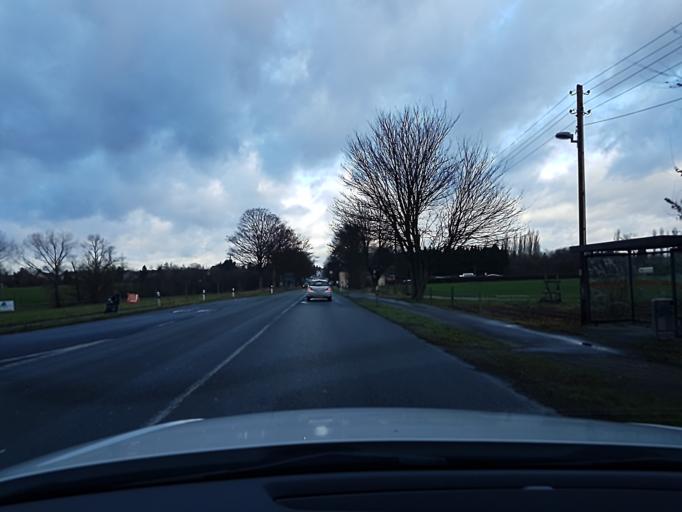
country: DE
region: North Rhine-Westphalia
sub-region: Regierungsbezirk Dusseldorf
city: Ratingen
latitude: 51.3609
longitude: 6.8632
